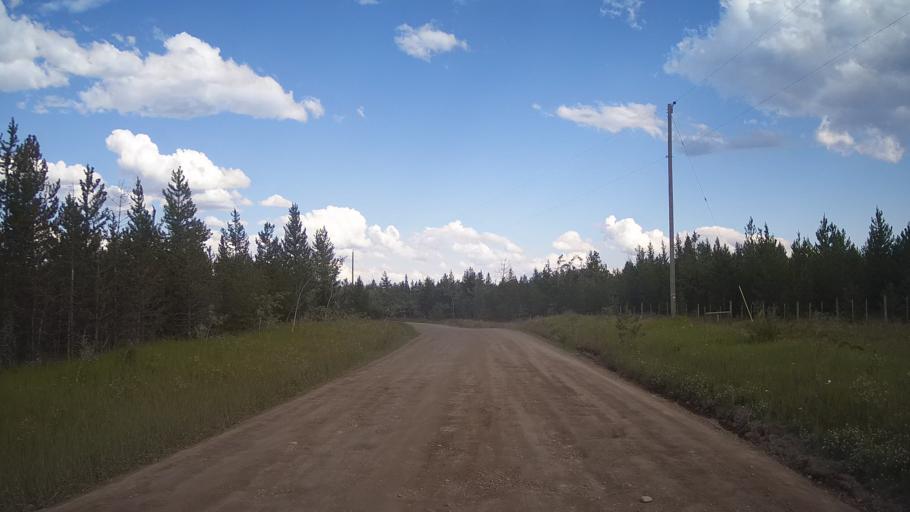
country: CA
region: British Columbia
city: Cache Creek
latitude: 51.2703
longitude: -121.7220
